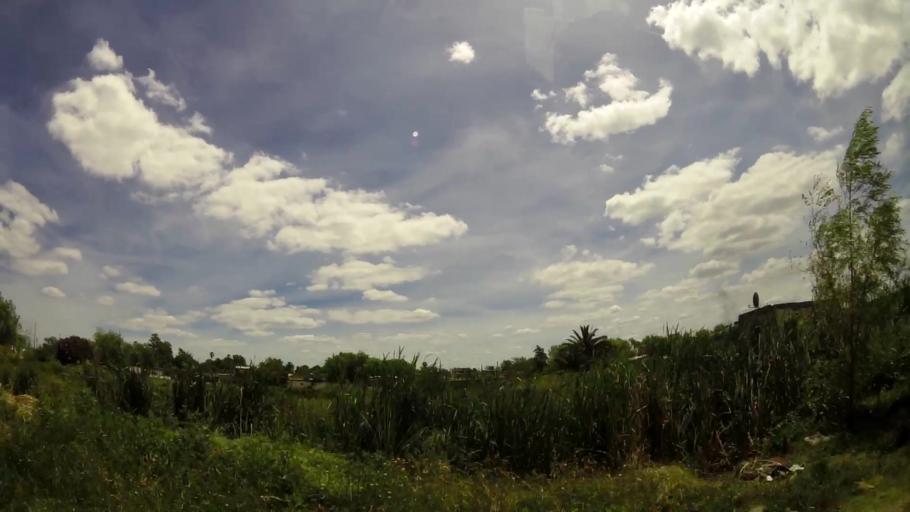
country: UY
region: Montevideo
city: Montevideo
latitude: -34.8654
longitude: -56.2460
